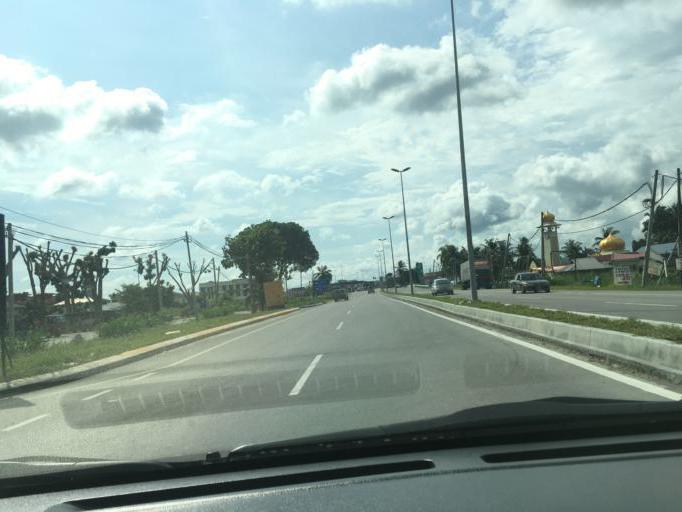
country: MY
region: Selangor
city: Batu Arang
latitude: 3.3127
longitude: 101.4190
